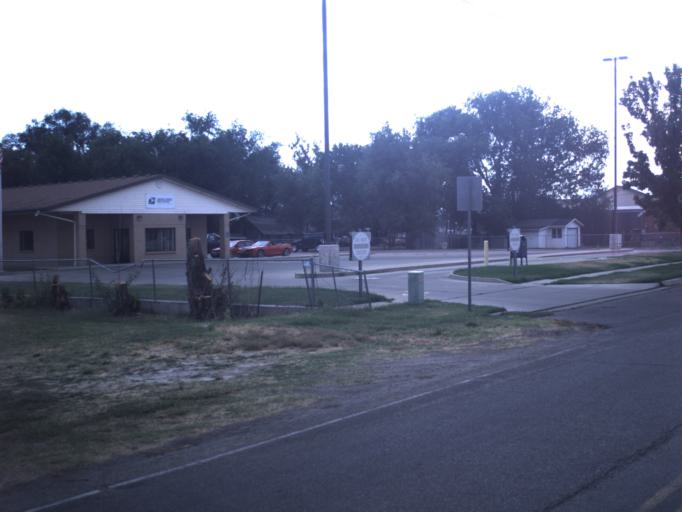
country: US
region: Utah
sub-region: Weber County
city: Hooper
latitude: 41.1639
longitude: -112.1245
